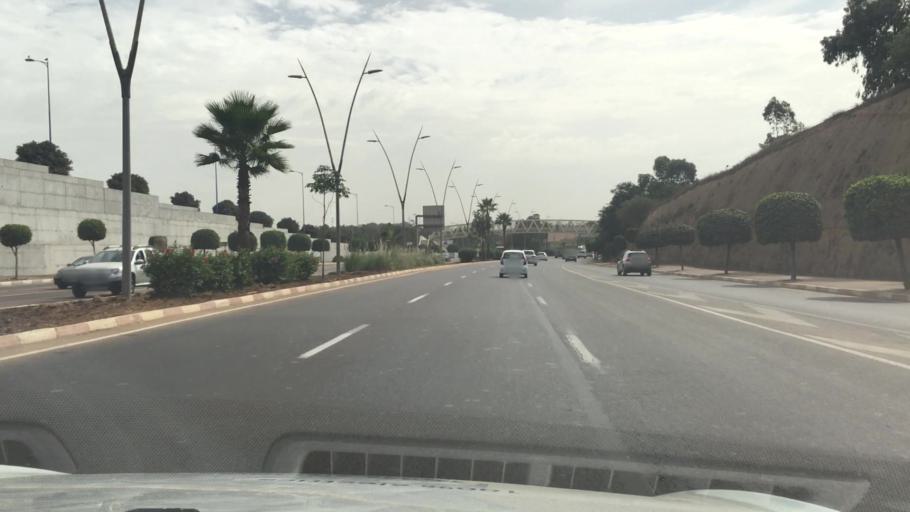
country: MA
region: Grand Casablanca
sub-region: Nouaceur
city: Bouskoura
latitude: 33.5170
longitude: -7.6321
